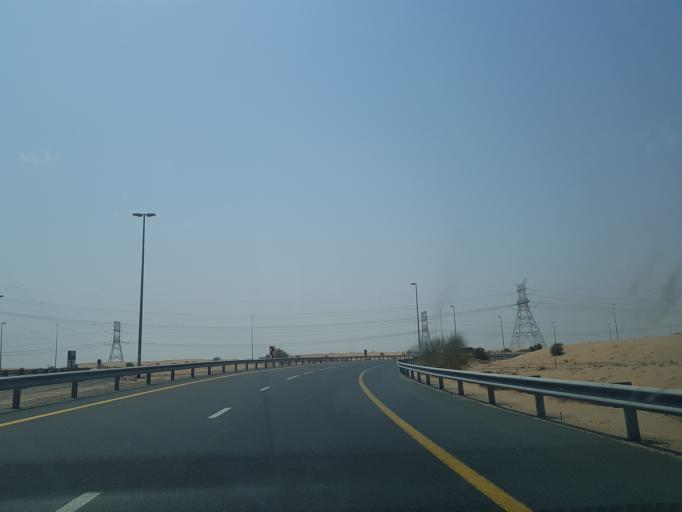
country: AE
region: Ash Shariqah
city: Sharjah
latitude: 25.1164
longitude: 55.4297
